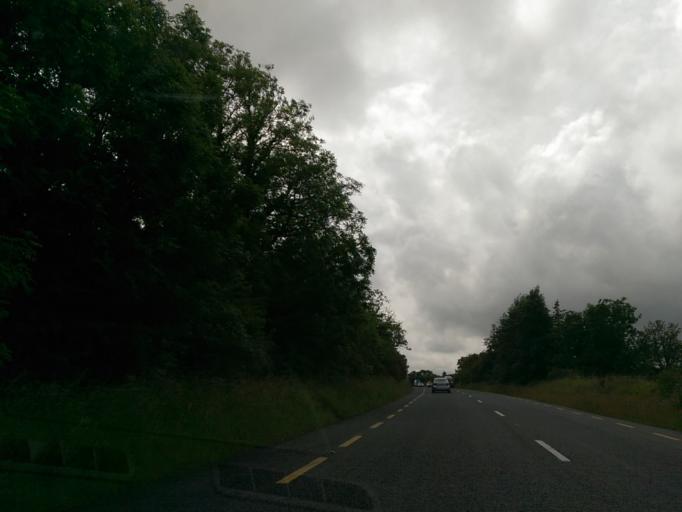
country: IE
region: Munster
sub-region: An Clar
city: Ennis
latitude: 52.7898
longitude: -9.0723
